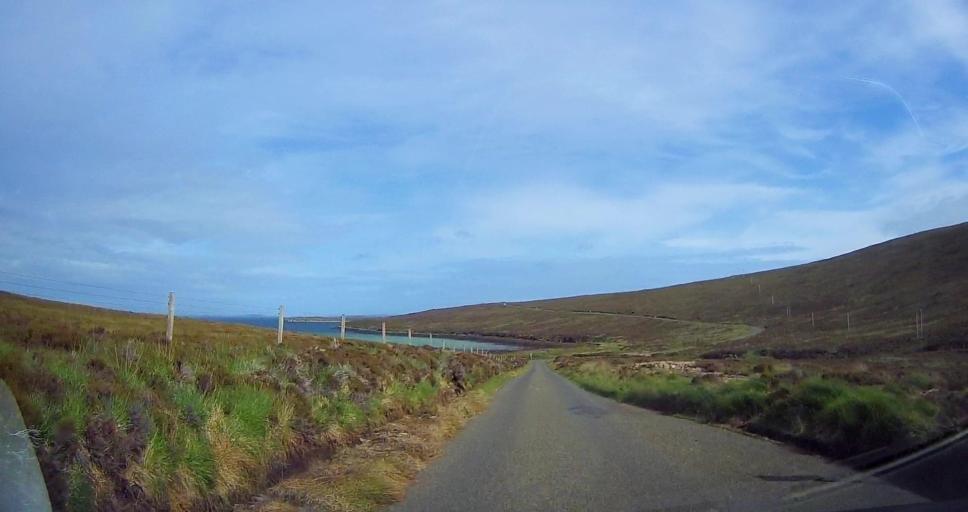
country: GB
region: Scotland
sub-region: Orkney Islands
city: Stromness
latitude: 58.8716
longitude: -3.2352
